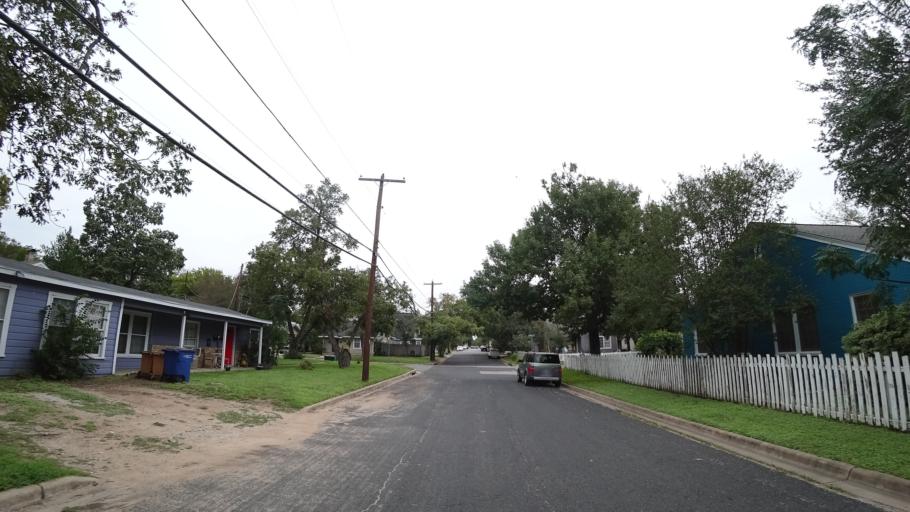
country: US
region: Texas
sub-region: Travis County
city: Austin
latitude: 30.3023
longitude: -97.7189
